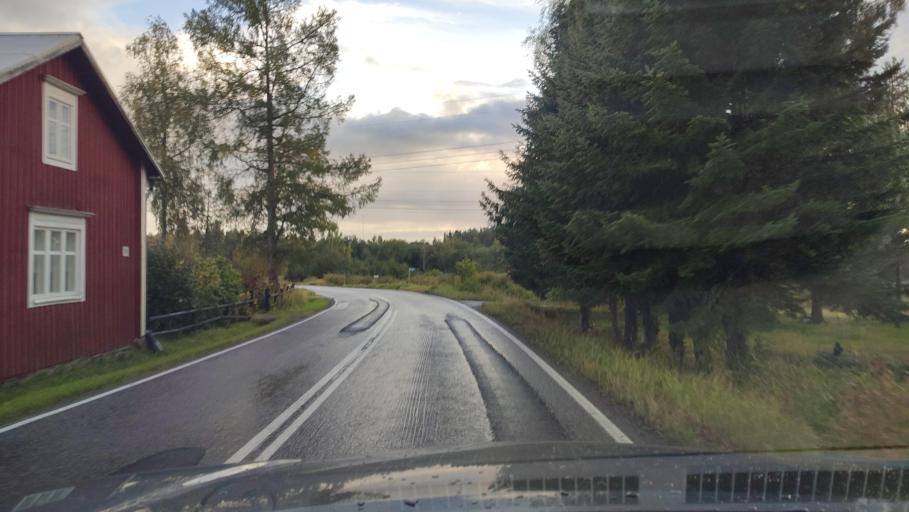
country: FI
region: Ostrobothnia
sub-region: Sydosterbotten
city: Kristinestad
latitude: 62.2842
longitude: 21.4194
